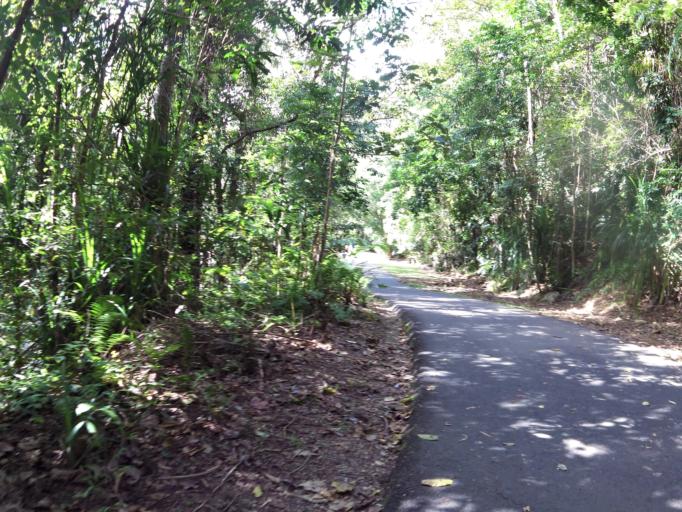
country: AU
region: Queensland
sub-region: Cairns
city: Woree
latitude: -16.9650
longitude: 145.6753
